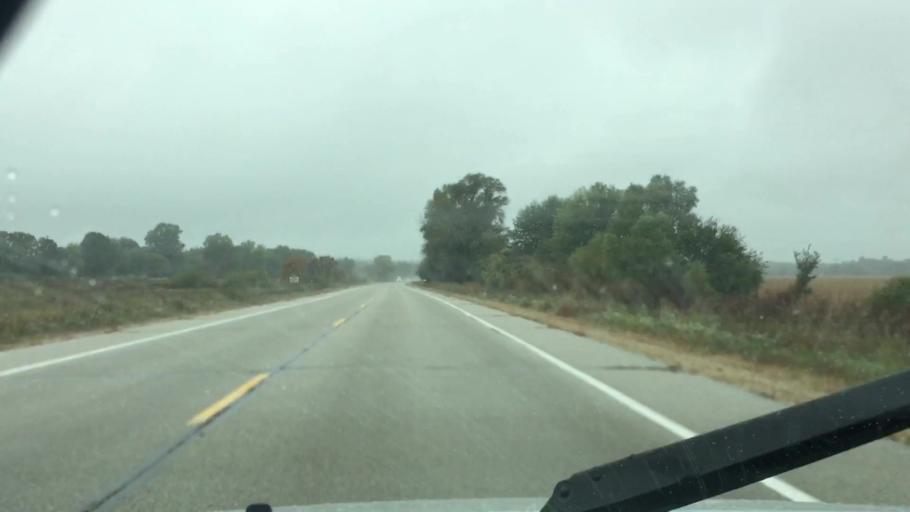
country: US
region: Wisconsin
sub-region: Waukesha County
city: Eagle
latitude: 42.8792
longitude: -88.5279
